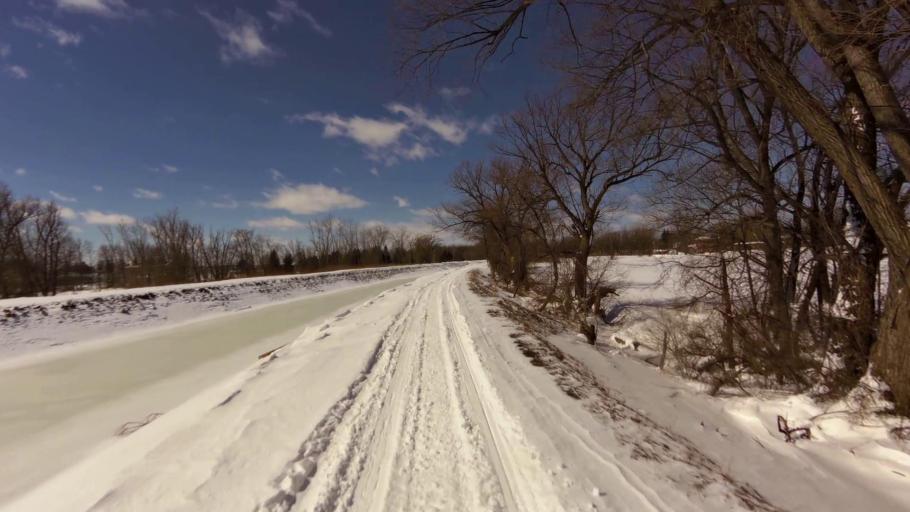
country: US
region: New York
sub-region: Orleans County
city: Albion
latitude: 43.2477
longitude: -78.2082
